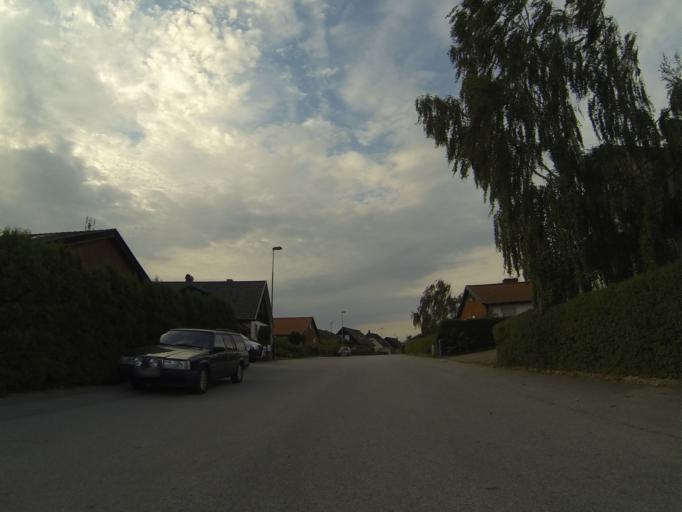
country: SE
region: Skane
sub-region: Lunds Kommun
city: Genarp
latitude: 55.6678
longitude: 13.3452
